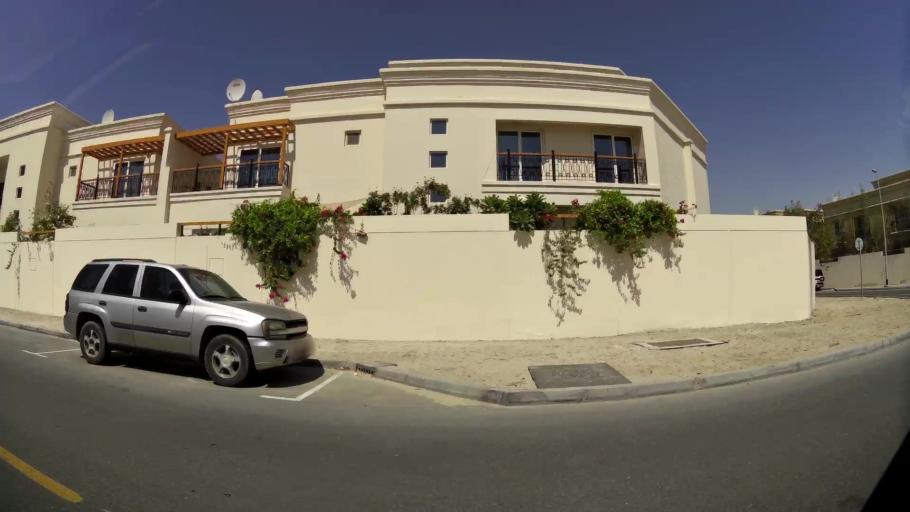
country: AE
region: Dubai
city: Dubai
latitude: 25.1087
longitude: 55.1997
